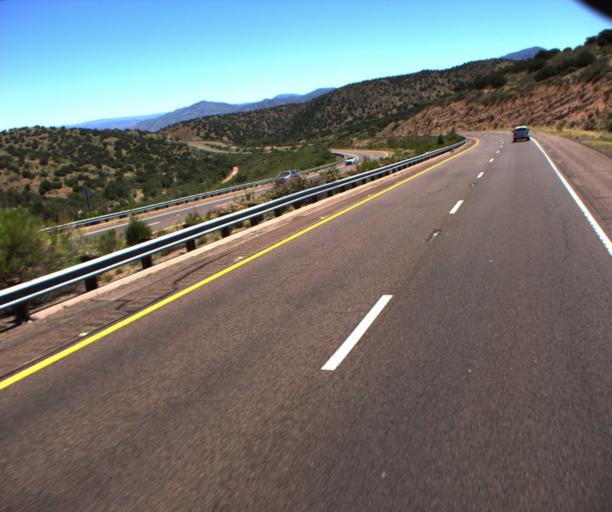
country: US
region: Arizona
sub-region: Gila County
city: Tonto Basin
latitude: 33.9966
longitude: -111.3658
